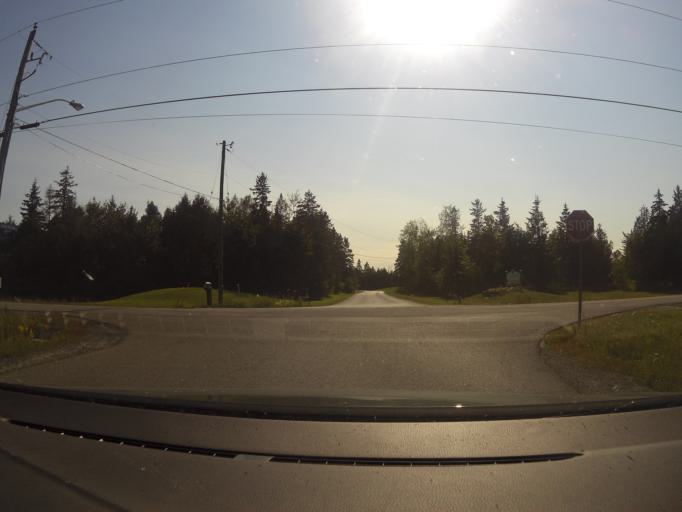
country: CA
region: Ontario
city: Carleton Place
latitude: 45.3057
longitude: -76.0802
